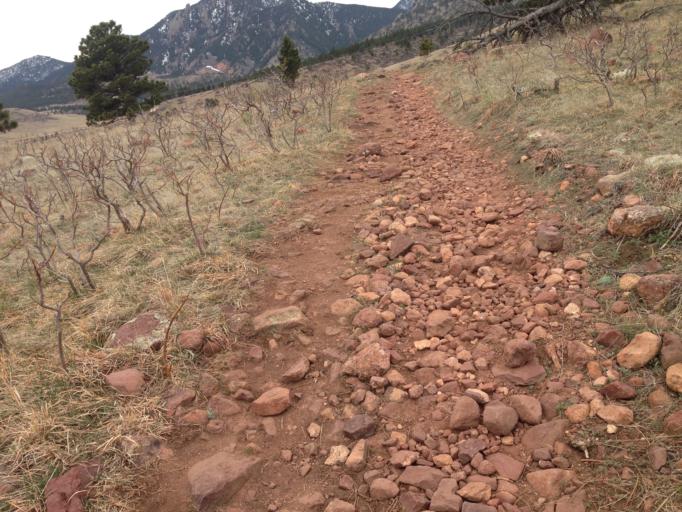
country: US
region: Colorado
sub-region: Boulder County
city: Boulder
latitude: 39.9466
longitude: -105.2590
